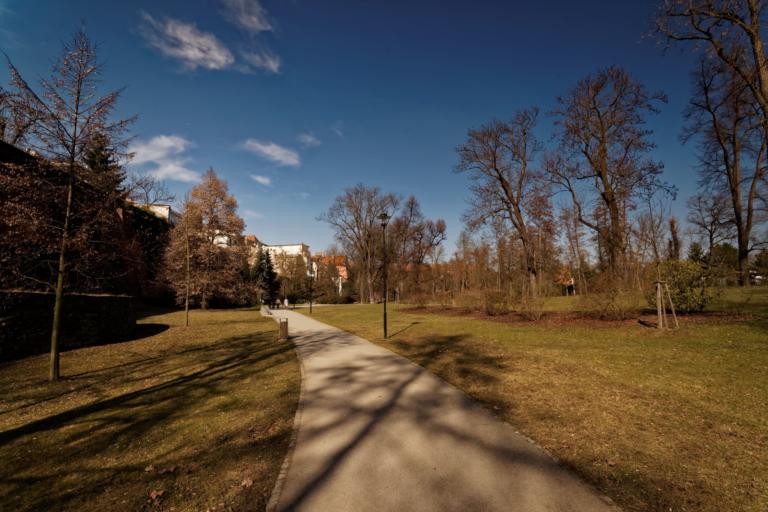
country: CZ
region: Olomoucky
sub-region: Okres Olomouc
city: Olomouc
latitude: 49.5916
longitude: 17.2560
